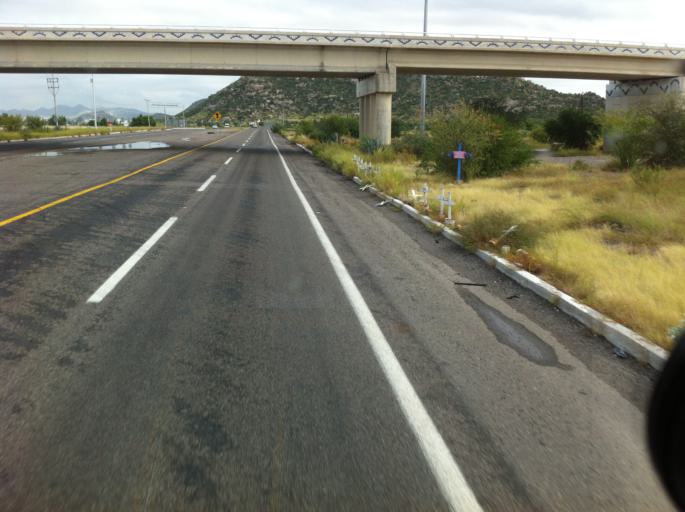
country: MX
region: Sonora
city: Hermosillo
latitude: 28.9947
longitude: -110.9715
